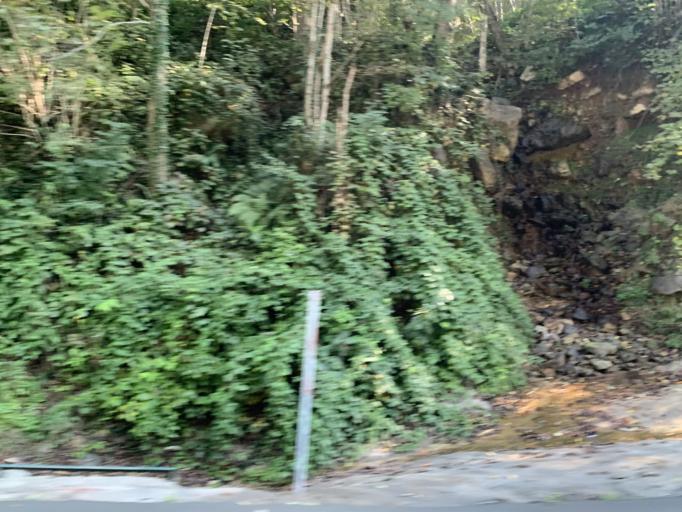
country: TR
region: Trabzon
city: Macka
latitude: 40.7050
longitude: 39.6501
